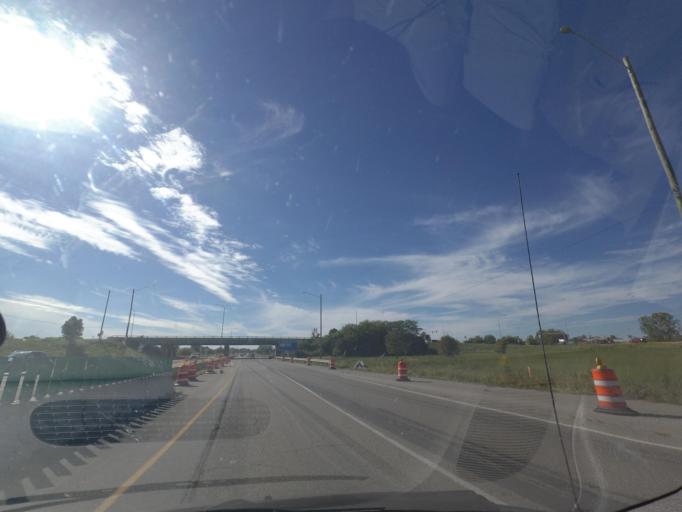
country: US
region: Illinois
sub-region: Champaign County
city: Champaign
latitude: 40.1344
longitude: -88.2421
